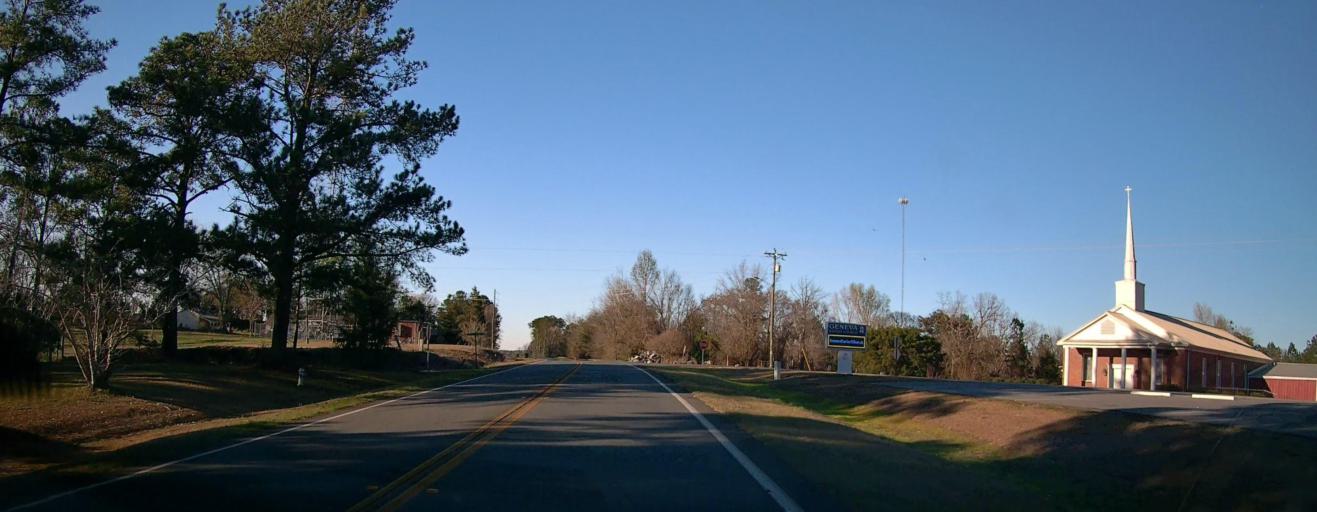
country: US
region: Georgia
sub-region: Talbot County
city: Talbotton
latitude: 32.5822
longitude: -84.5530
